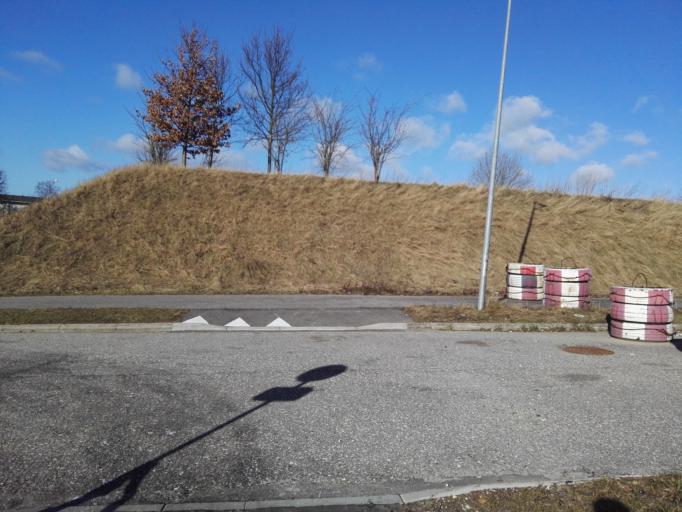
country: DK
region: Capital Region
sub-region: Egedal Kommune
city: Stenlose
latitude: 55.7862
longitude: 12.1818
